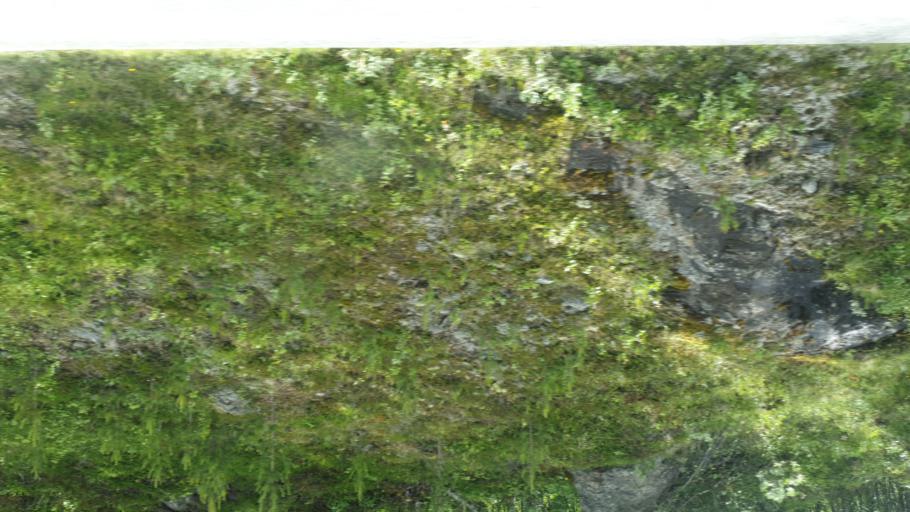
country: NO
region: Oppland
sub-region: Vaga
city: Vagamo
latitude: 61.7504
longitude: 9.0793
